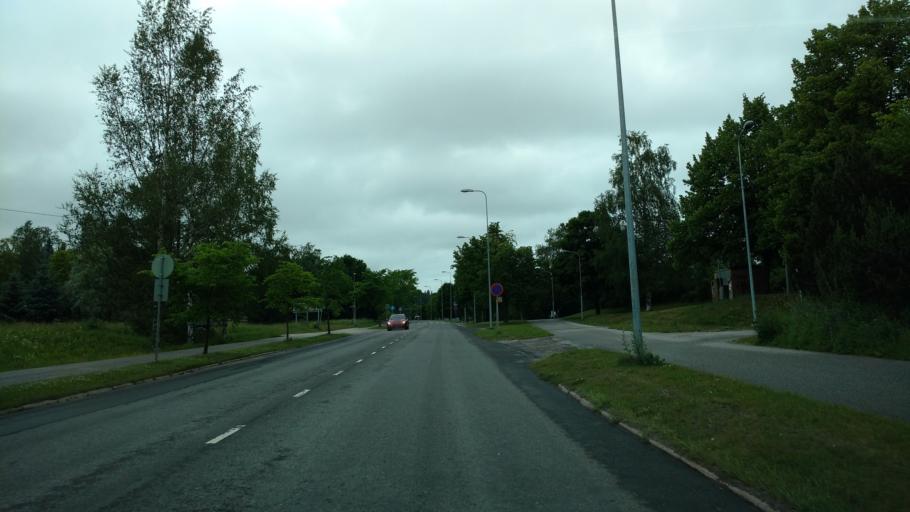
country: FI
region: Varsinais-Suomi
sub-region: Salo
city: Halikko
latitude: 60.3940
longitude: 23.1072
